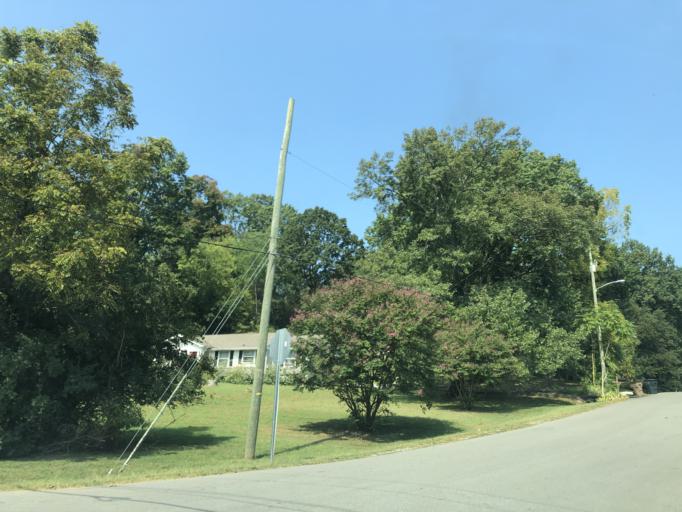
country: US
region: Tennessee
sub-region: Davidson County
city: Lakewood
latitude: 36.1542
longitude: -86.6481
